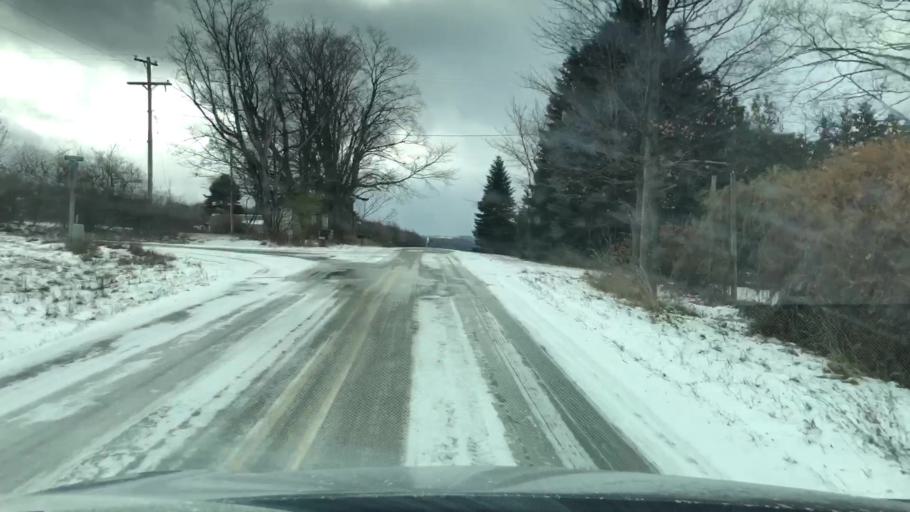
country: US
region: Michigan
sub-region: Antrim County
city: Elk Rapids
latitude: 44.9359
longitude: -85.5156
